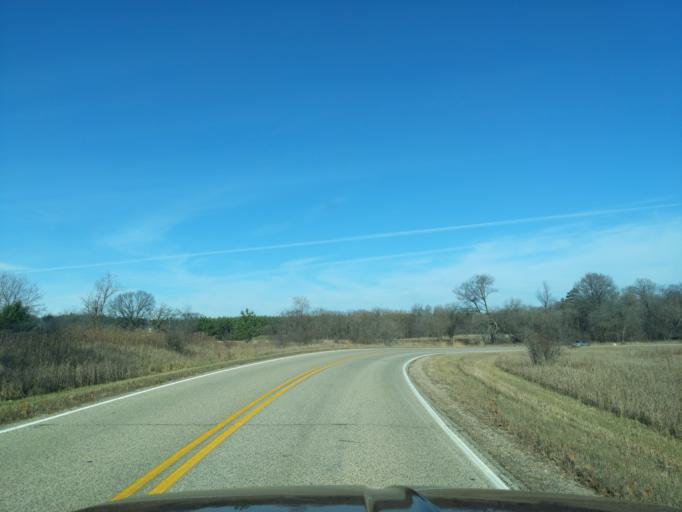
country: US
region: Wisconsin
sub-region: Waushara County
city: Silver Lake
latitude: 44.1182
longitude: -89.1763
